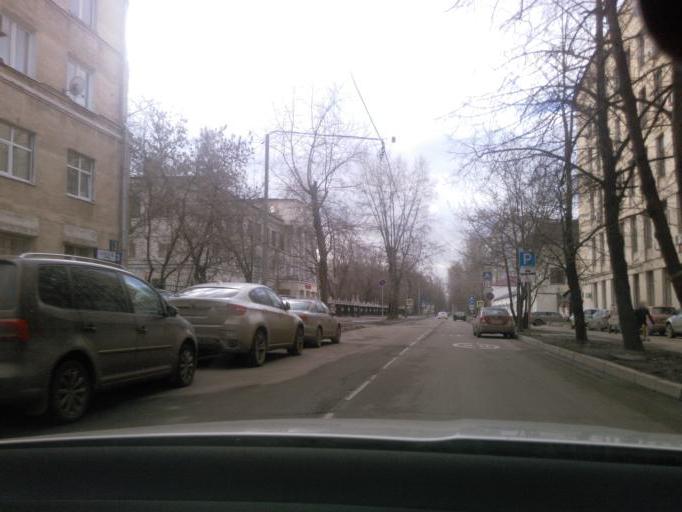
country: RU
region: Moscow
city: Zamoskvorech'ye
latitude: 55.7184
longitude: 37.6137
